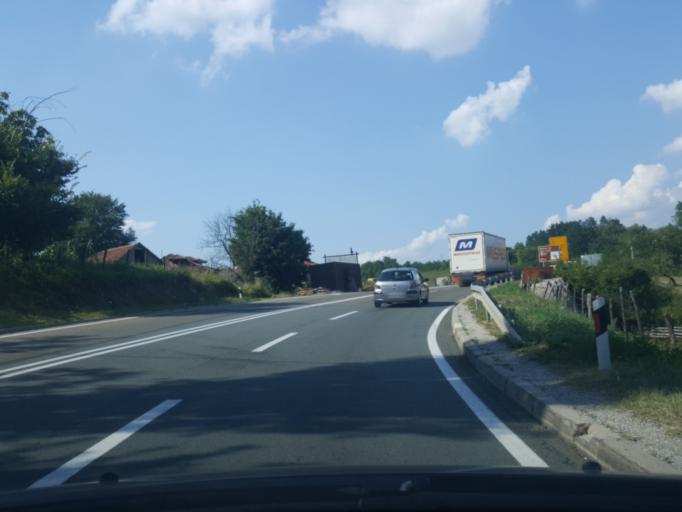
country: RS
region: Central Serbia
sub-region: Moravicki Okrug
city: Gornji Milanovac
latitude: 44.1193
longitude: 20.4826
